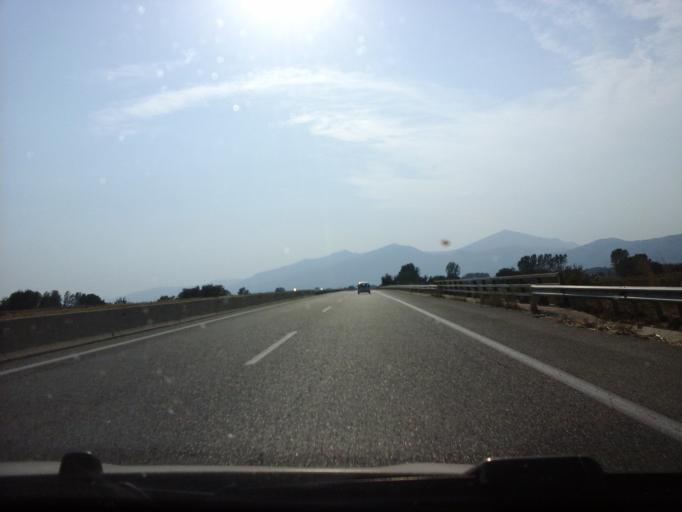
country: GR
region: East Macedonia and Thrace
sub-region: Nomos Xanthis
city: Selero
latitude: 41.1177
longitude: 25.0022
